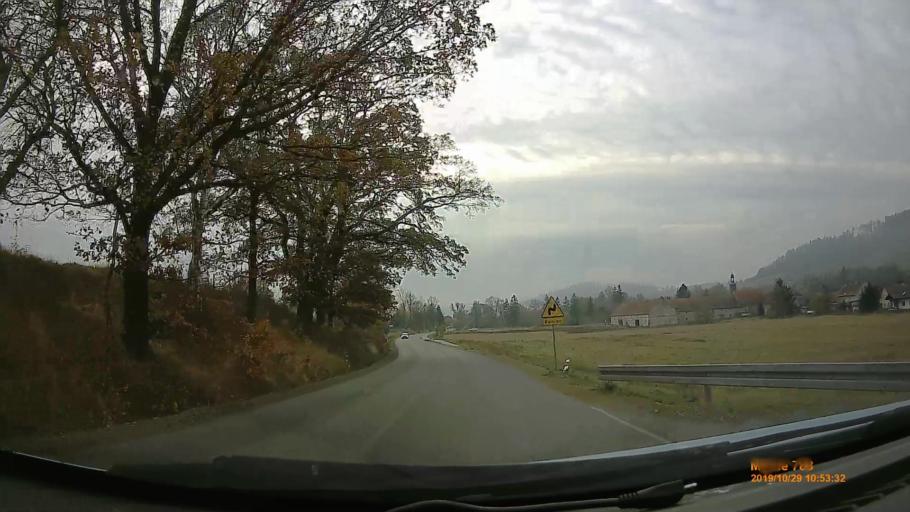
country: PL
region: Lower Silesian Voivodeship
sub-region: Powiat klodzki
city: Nowa Ruda
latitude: 50.5305
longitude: 16.4827
